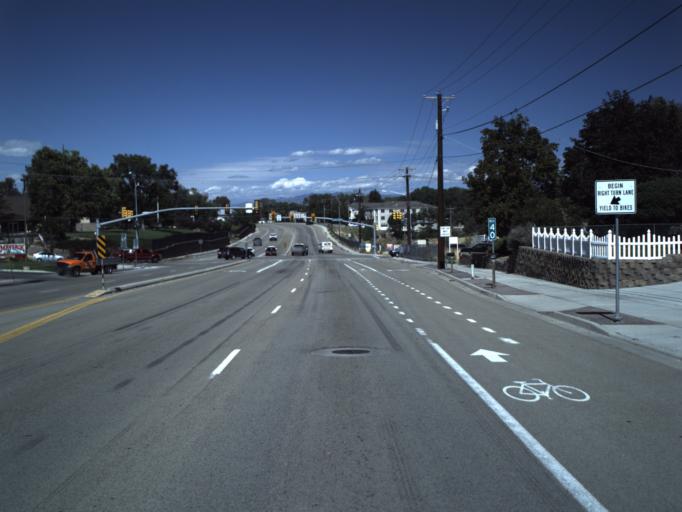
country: US
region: Utah
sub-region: Salt Lake County
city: Bluffdale
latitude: 40.4885
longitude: -111.9404
